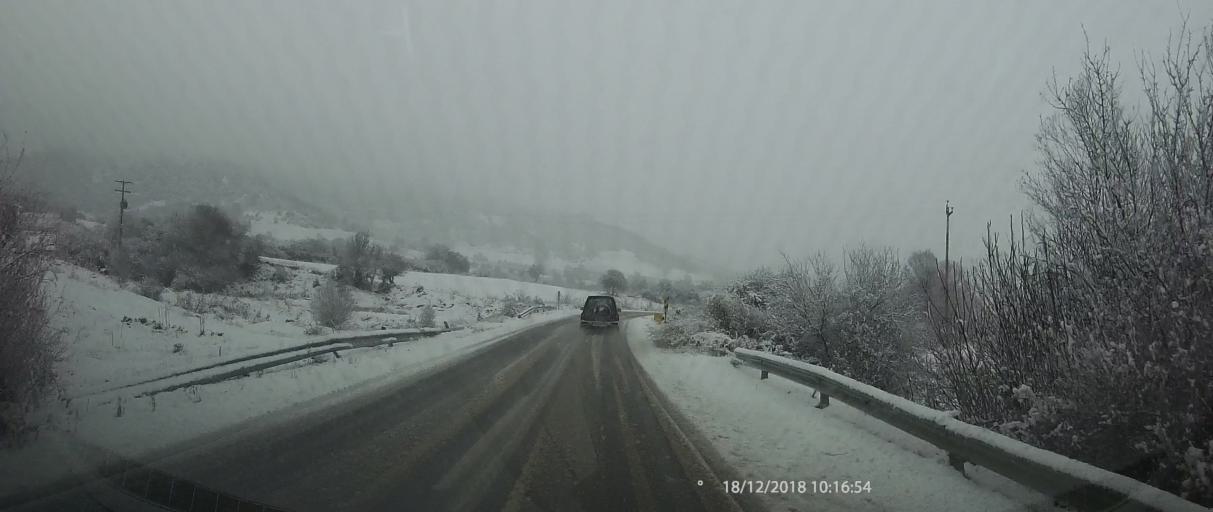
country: GR
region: Thessaly
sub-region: Nomos Larisis
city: Livadi
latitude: 40.1199
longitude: 22.2107
